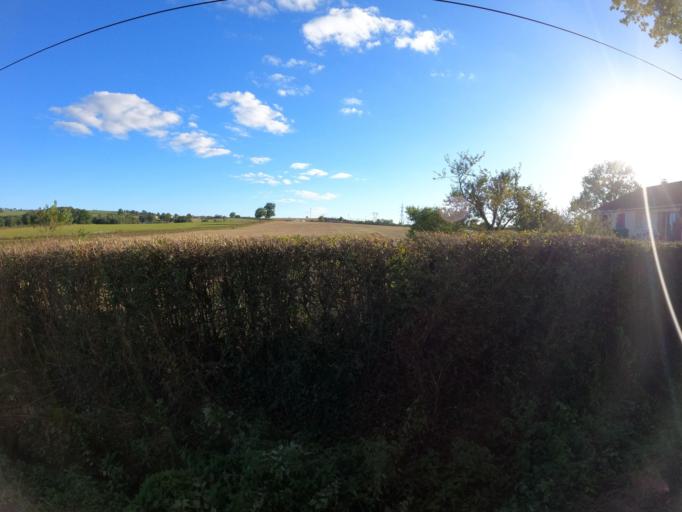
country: FR
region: Bourgogne
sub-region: Departement de Saone-et-Loire
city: Saint-Leu
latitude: 46.7536
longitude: 4.5094
